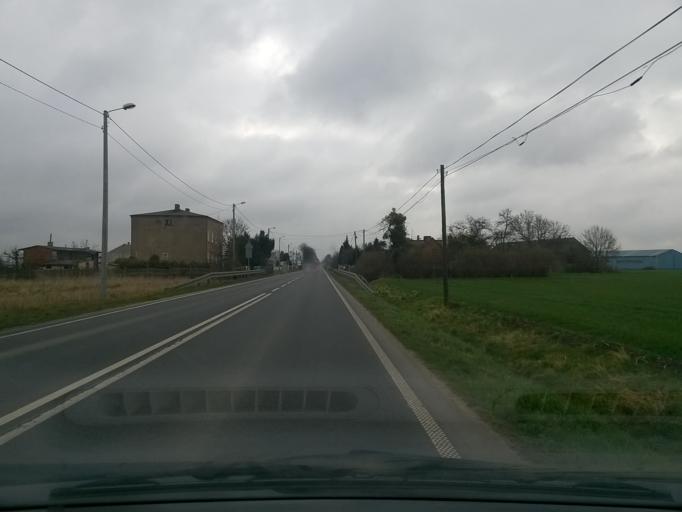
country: PL
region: Kujawsko-Pomorskie
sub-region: Powiat nakielski
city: Kcynia
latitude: 52.9908
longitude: 17.5168
